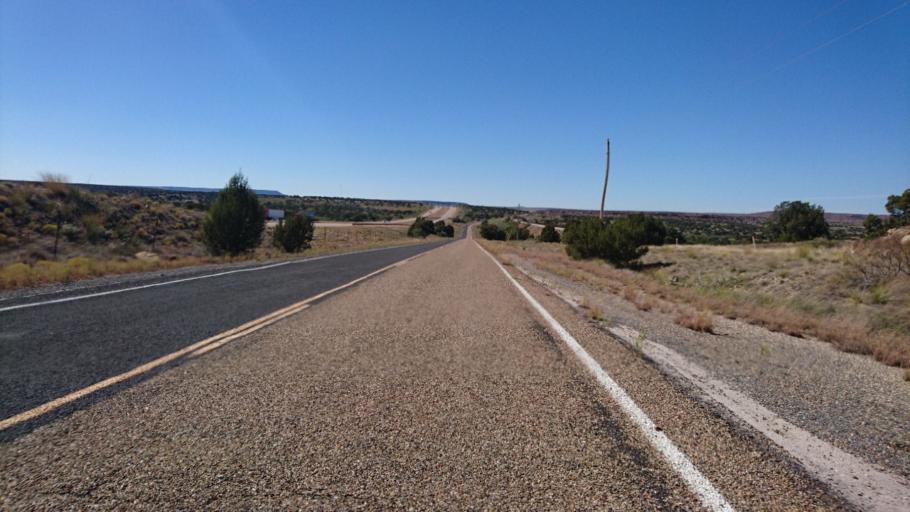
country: US
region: New Mexico
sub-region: Quay County
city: Tucumcari
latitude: 35.0687
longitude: -104.2030
